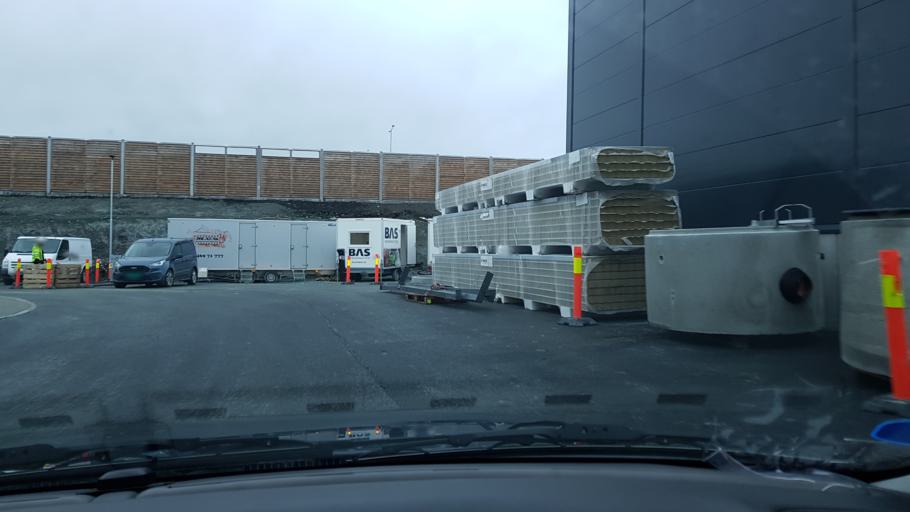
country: NO
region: Sor-Trondelag
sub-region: Trondheim
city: Trondheim
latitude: 63.3375
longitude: 10.3623
